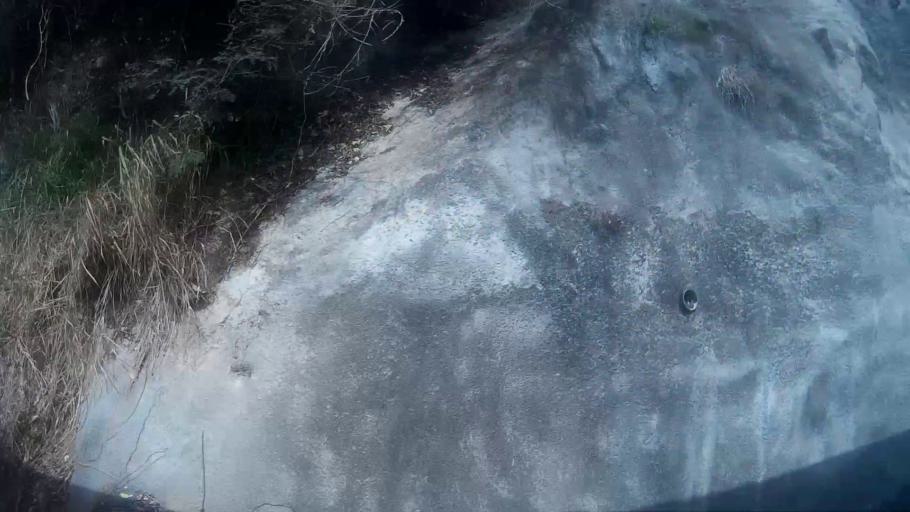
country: VN
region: Khanh Hoa
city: Van Gia
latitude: 12.8423
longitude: 109.3870
